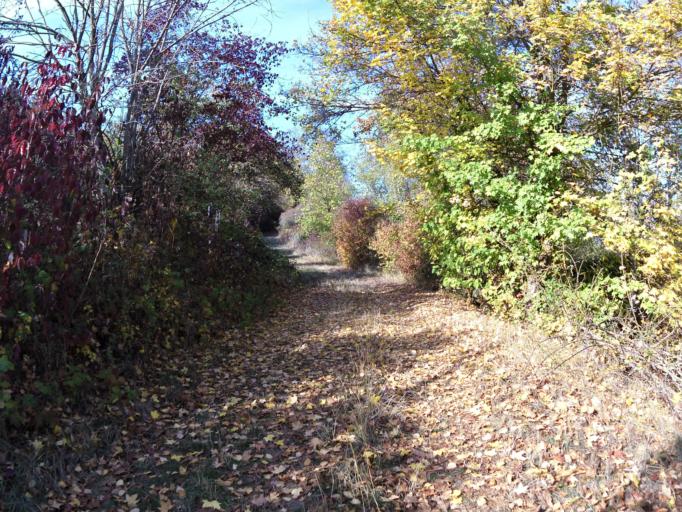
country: DE
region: Bavaria
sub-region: Regierungsbezirk Unterfranken
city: Eibelstadt
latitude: 49.7174
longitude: 9.9919
